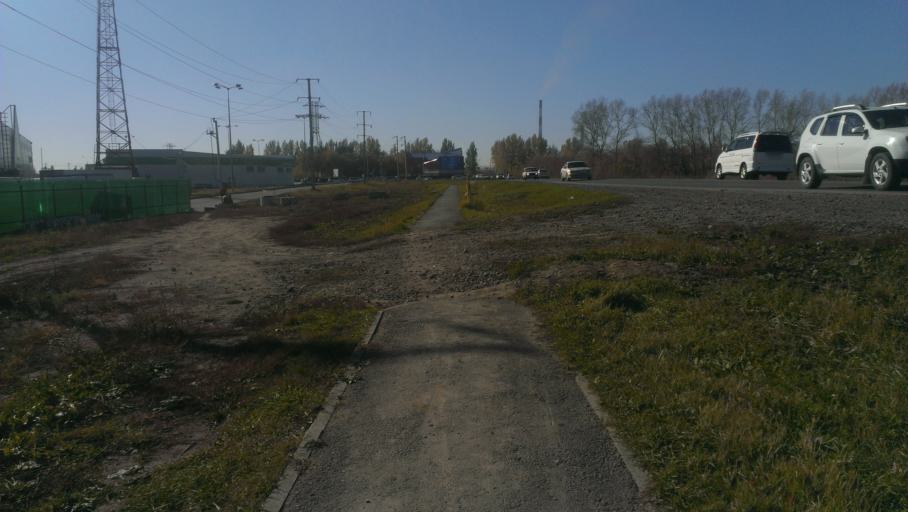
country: RU
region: Altai Krai
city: Novosilikatnyy
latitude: 53.3515
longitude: 83.6315
